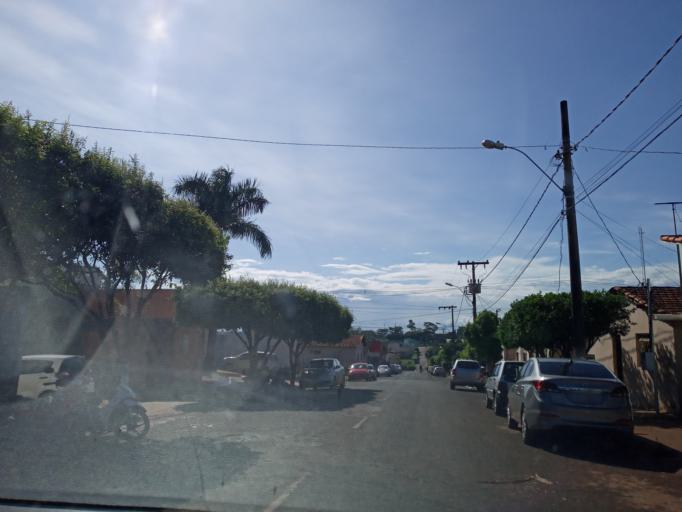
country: BR
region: Goias
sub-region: Itumbiara
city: Itumbiara
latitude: -18.4377
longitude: -49.1839
